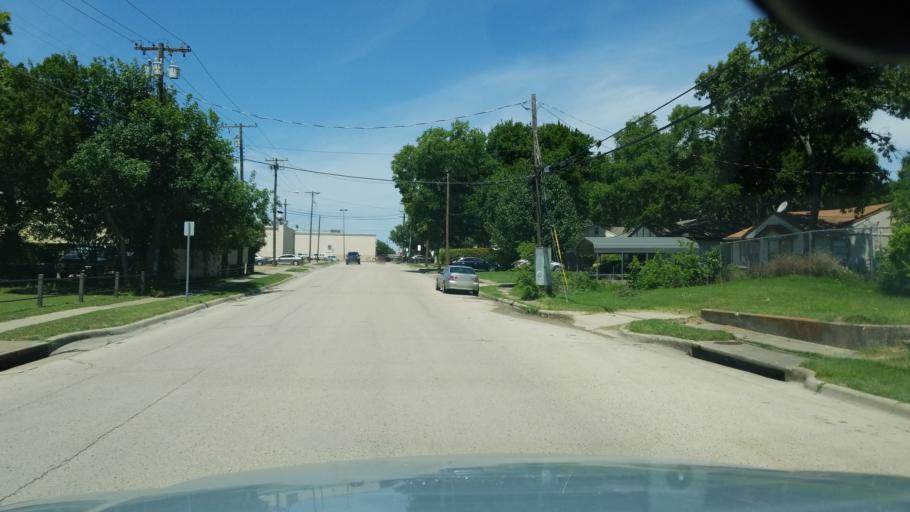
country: US
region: Texas
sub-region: Dallas County
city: Irving
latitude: 32.8132
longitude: -96.9326
